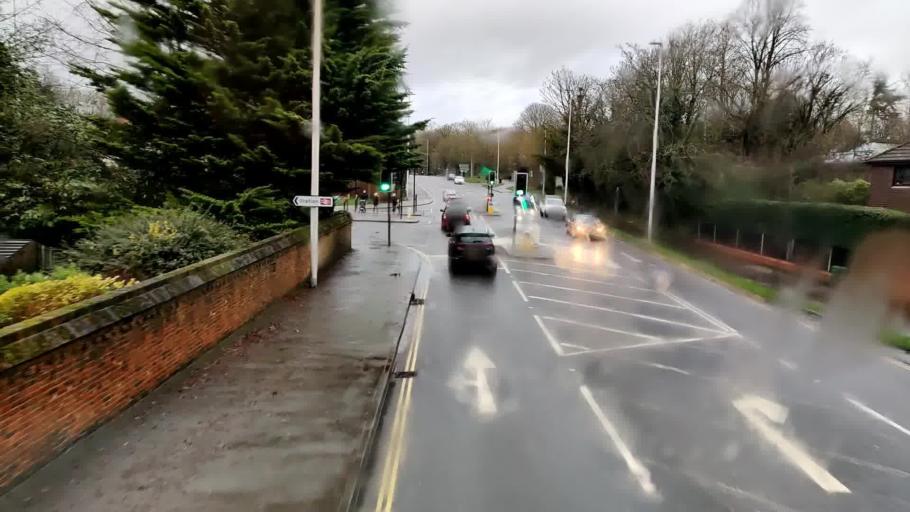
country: GB
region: England
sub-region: Wokingham
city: Wokingham
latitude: 51.4135
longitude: -0.8412
